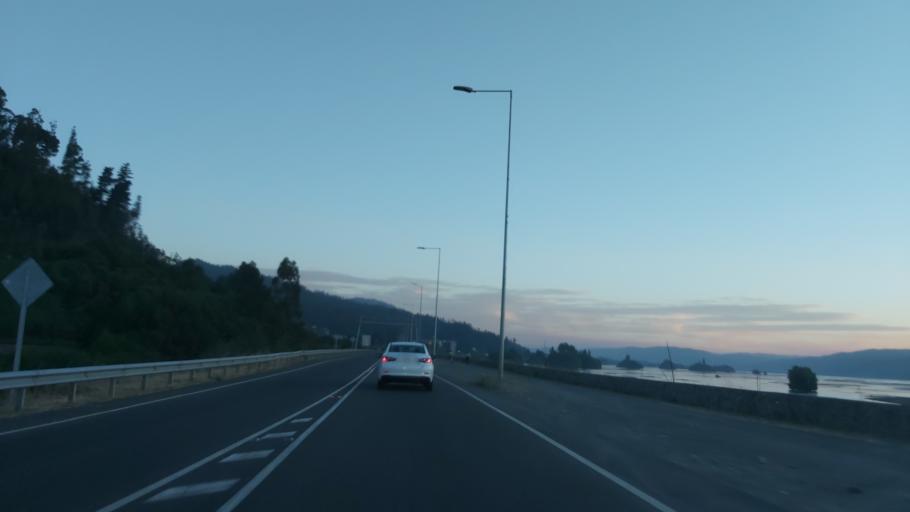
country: CL
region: Biobio
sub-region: Provincia de Concepcion
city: Concepcion
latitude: -36.8718
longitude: -73.0435
